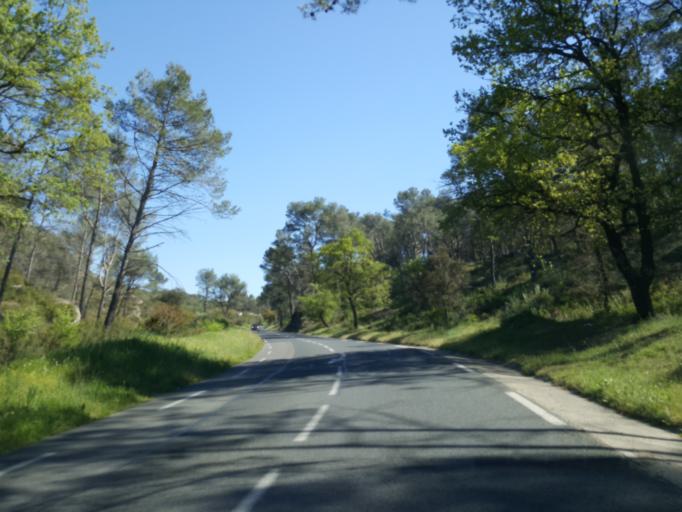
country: FR
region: Provence-Alpes-Cote d'Azur
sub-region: Departement des Bouches-du-Rhone
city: Cabries
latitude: 43.4354
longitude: 5.3634
